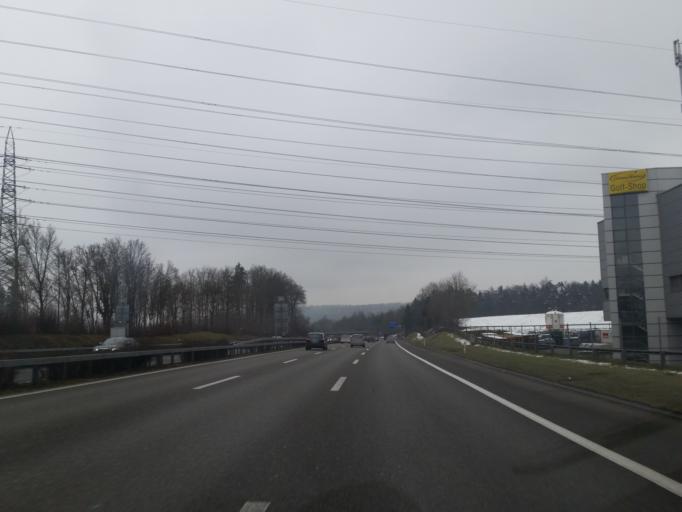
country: CH
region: Zurich
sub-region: Bezirk Pfaeffikon
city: Effretikon
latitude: 47.4398
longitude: 8.6869
